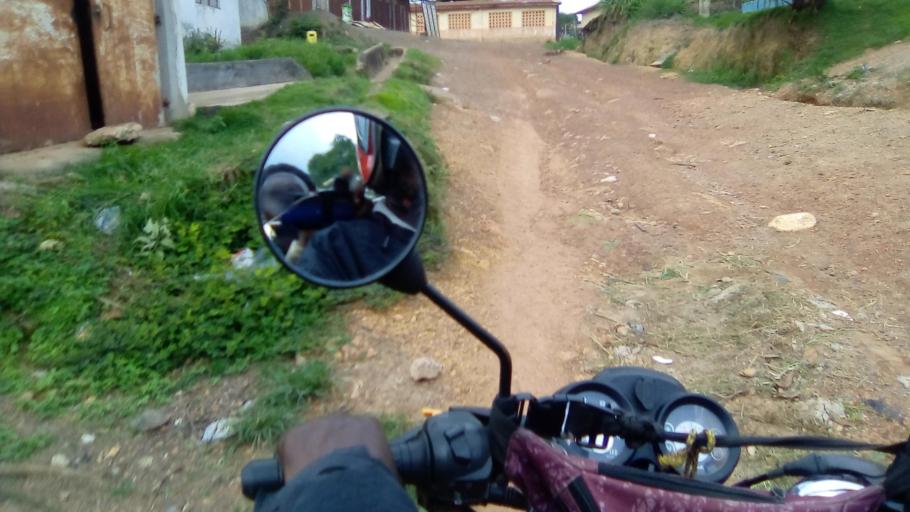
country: SL
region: Southern Province
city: Bo
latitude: 7.9578
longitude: -11.7295
